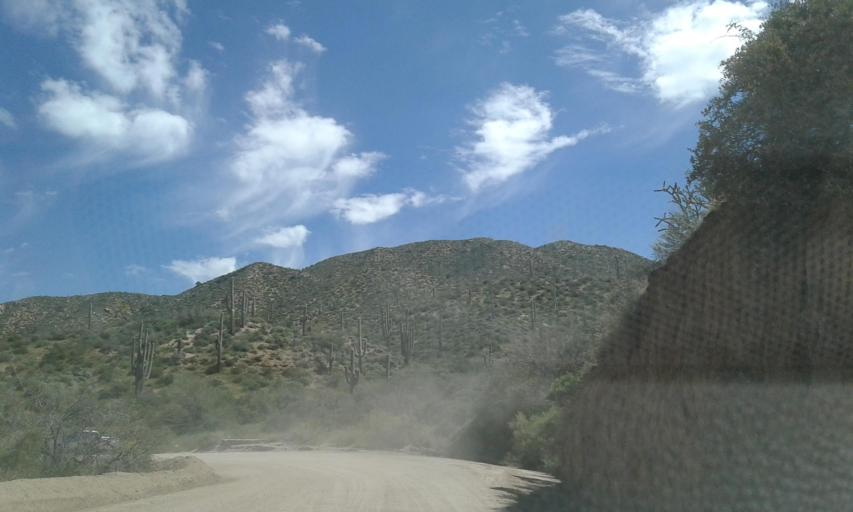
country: US
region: Arizona
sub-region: Gila County
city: Tonto Basin
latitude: 33.5665
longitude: -111.2368
